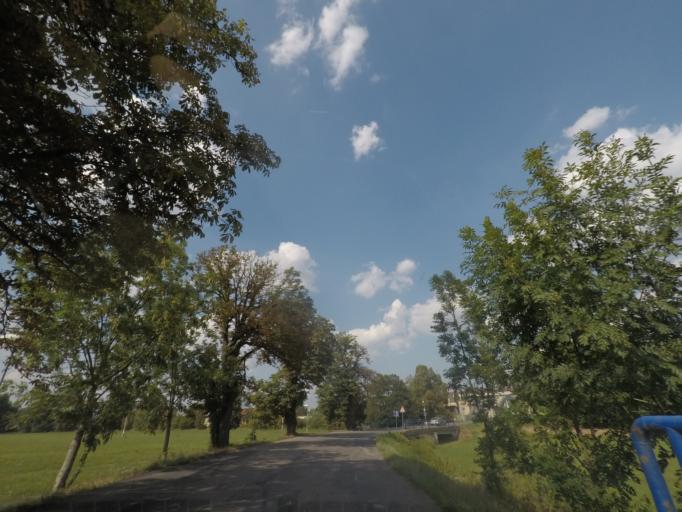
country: CZ
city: Albrechtice nad Orlici
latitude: 50.1478
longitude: 16.0661
